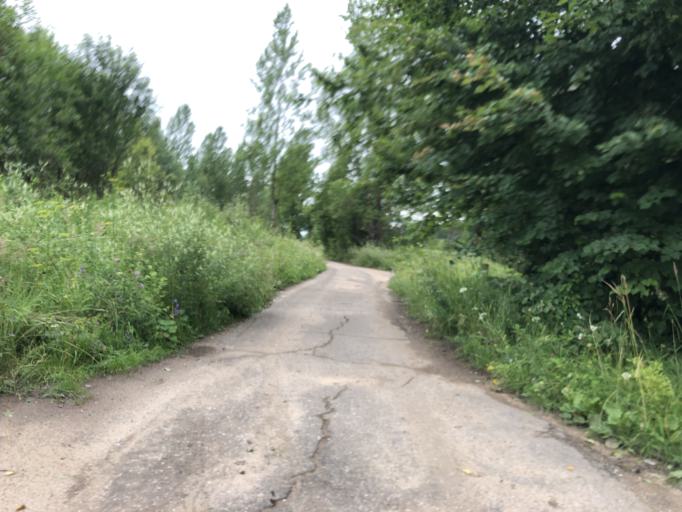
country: RU
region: Tverskaya
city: Rzhev
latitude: 56.2436
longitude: 34.3743
